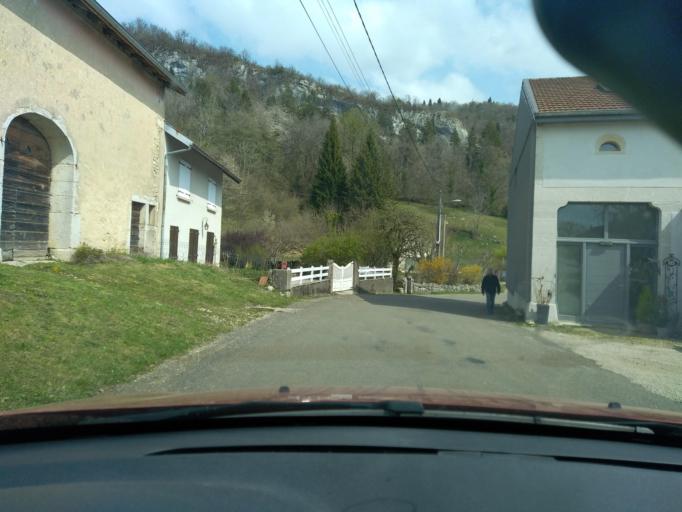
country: FR
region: Franche-Comte
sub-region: Departement du Jura
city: Moirans-en-Montagne
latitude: 46.4574
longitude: 5.7380
